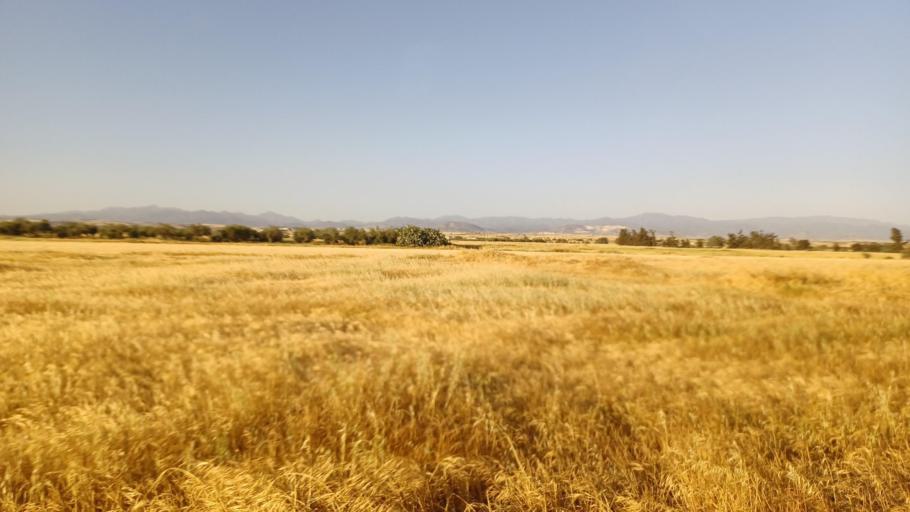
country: CY
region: Lefkosia
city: Kokkinotrimithia
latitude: 35.1425
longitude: 33.1899
